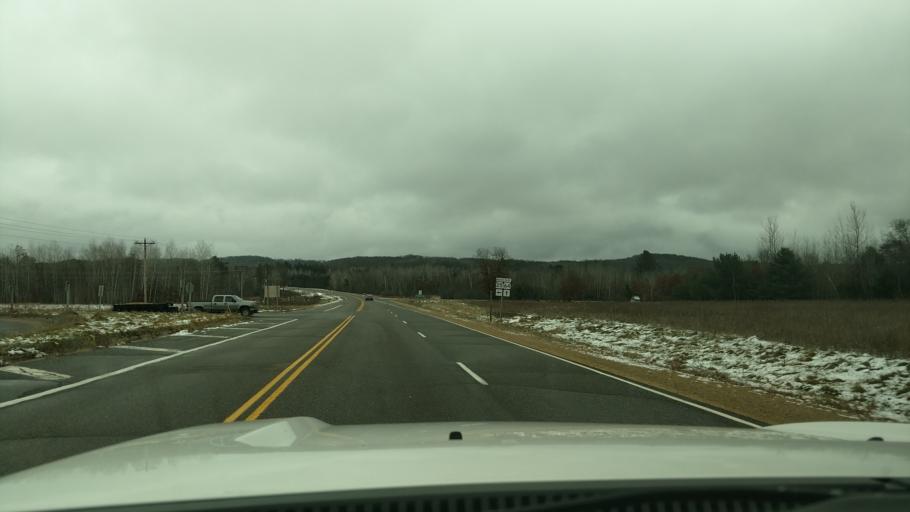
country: US
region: Wisconsin
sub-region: Dunn County
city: Tainter Lake
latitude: 45.1228
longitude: -91.8951
